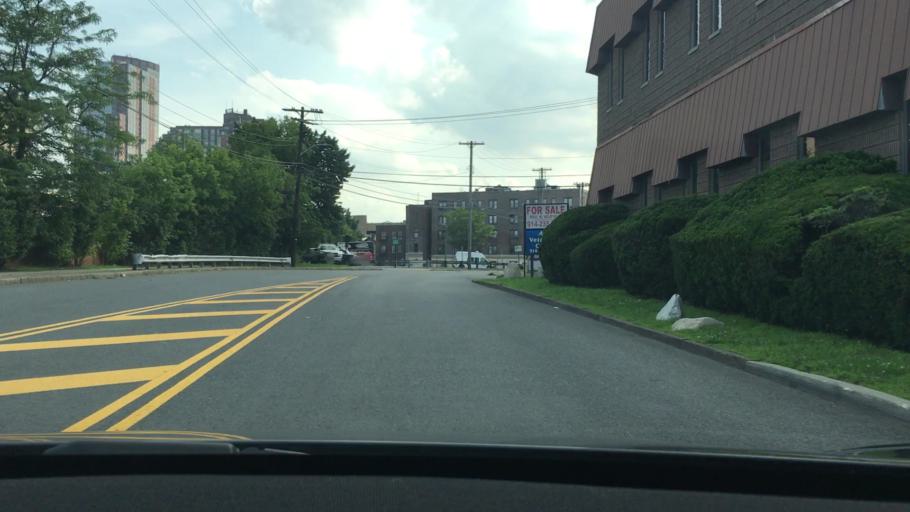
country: US
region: New York
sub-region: Westchester County
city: New Rochelle
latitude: 40.9146
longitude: -73.7818
